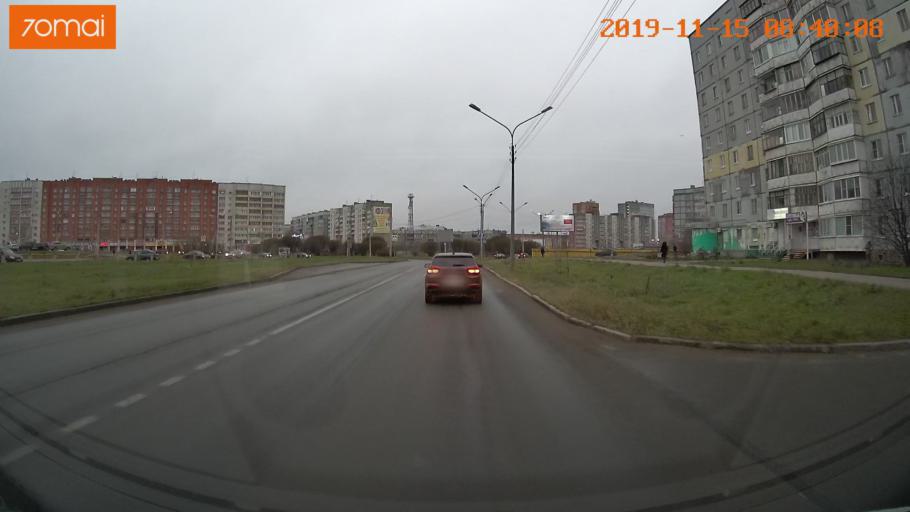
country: RU
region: Vologda
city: Cherepovets
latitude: 59.0939
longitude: 37.9174
